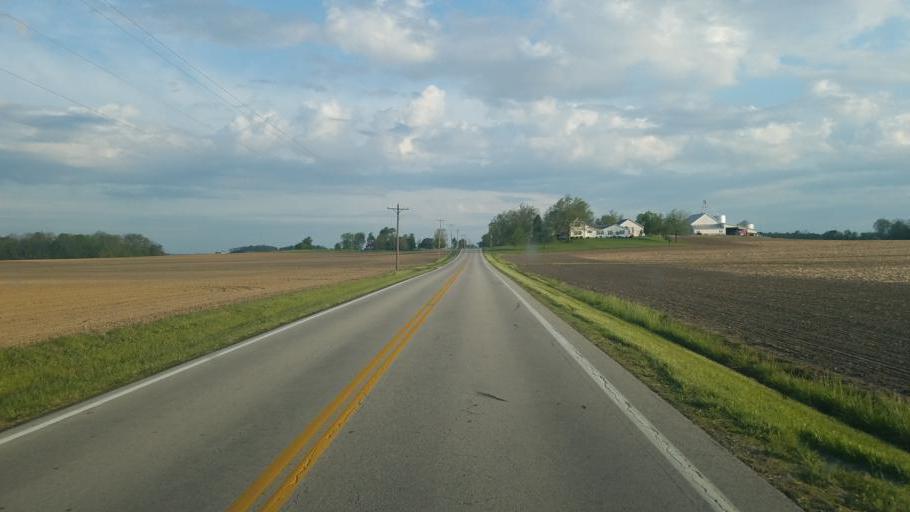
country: US
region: Ohio
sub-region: Clinton County
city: Sabina
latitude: 39.4111
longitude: -83.6104
